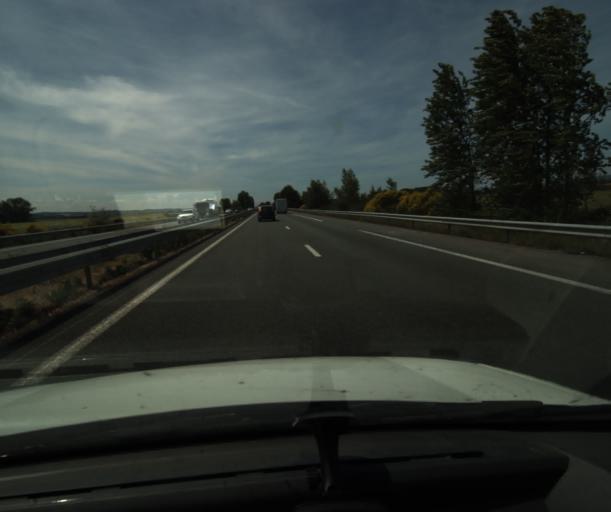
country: FR
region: Languedoc-Roussillon
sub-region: Departement de l'Aude
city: Bram
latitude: 43.2424
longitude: 2.0797
